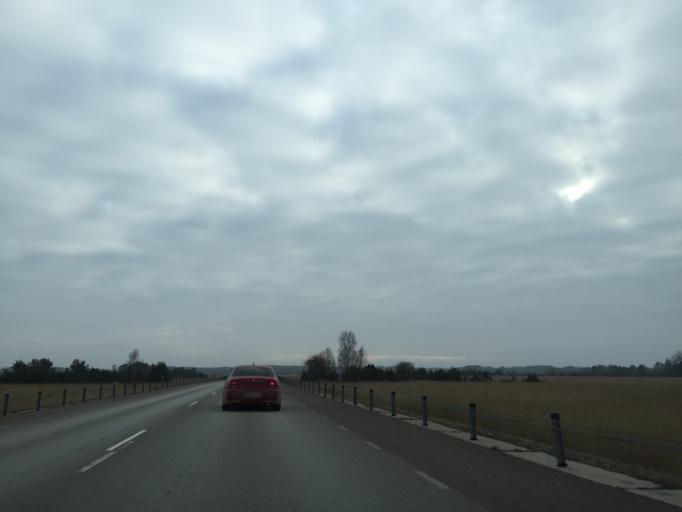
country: EE
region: Saare
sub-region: Orissaare vald
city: Orissaare
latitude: 58.5439
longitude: 23.1291
